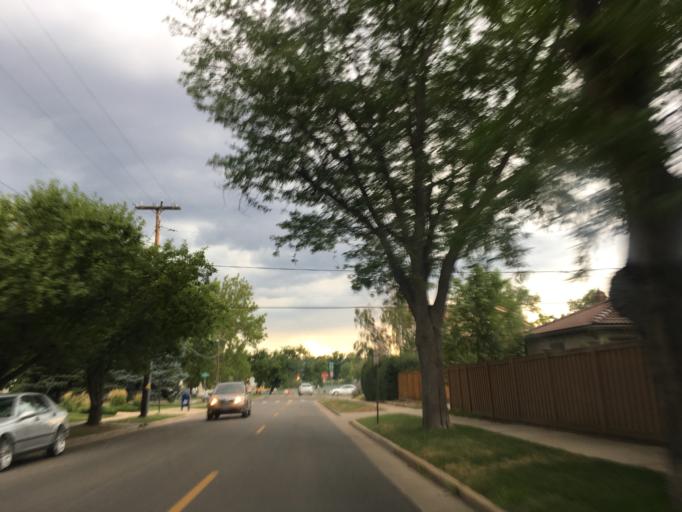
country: US
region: Colorado
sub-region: Arapahoe County
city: Glendale
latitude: 39.7039
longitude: -104.9675
